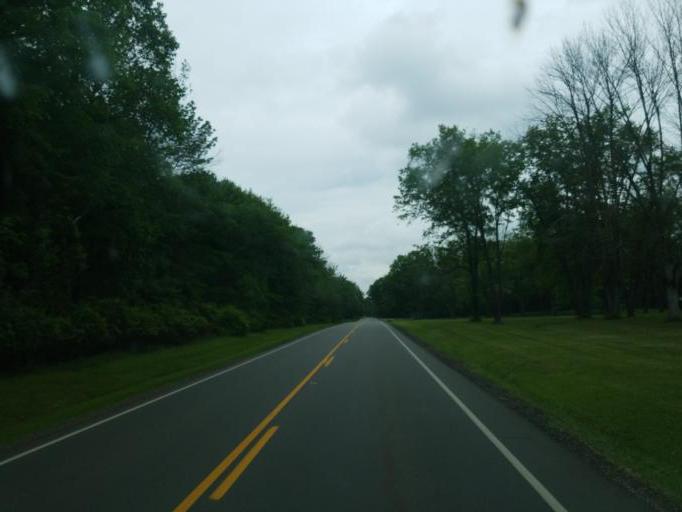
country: US
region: Ohio
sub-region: Richland County
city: Lexington
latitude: 40.7041
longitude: -82.6377
